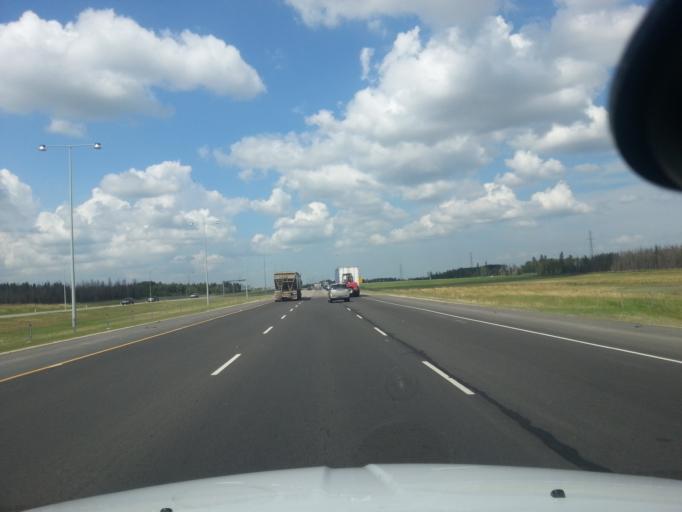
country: CA
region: Alberta
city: St. Albert
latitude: 53.5508
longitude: -113.6587
